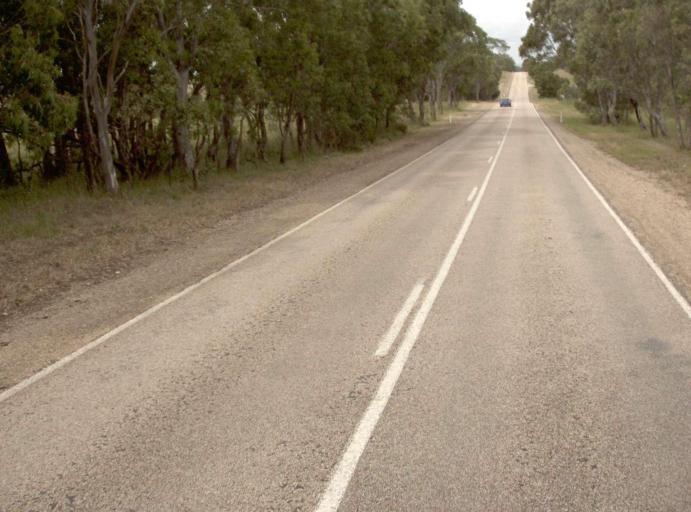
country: AU
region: Victoria
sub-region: Wellington
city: Sale
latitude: -37.9402
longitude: 147.0933
